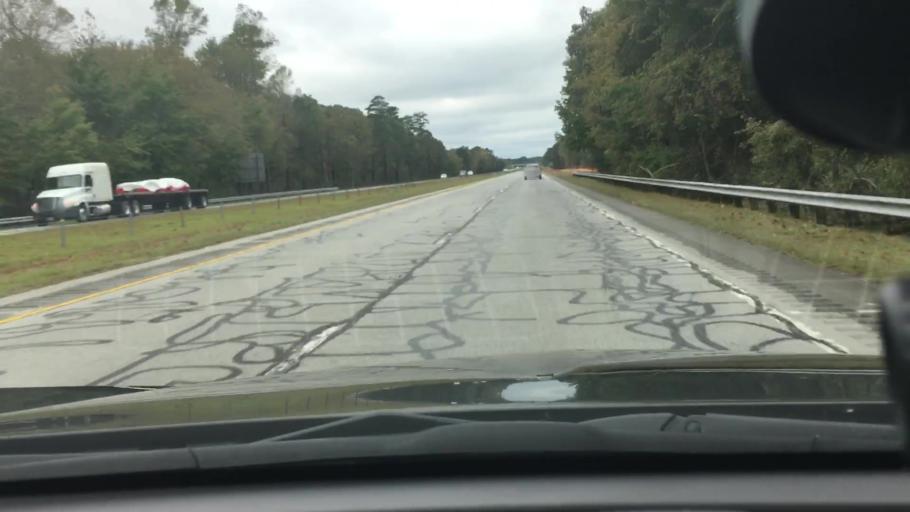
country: US
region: North Carolina
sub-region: Pitt County
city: Farmville
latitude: 35.6153
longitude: -77.6247
